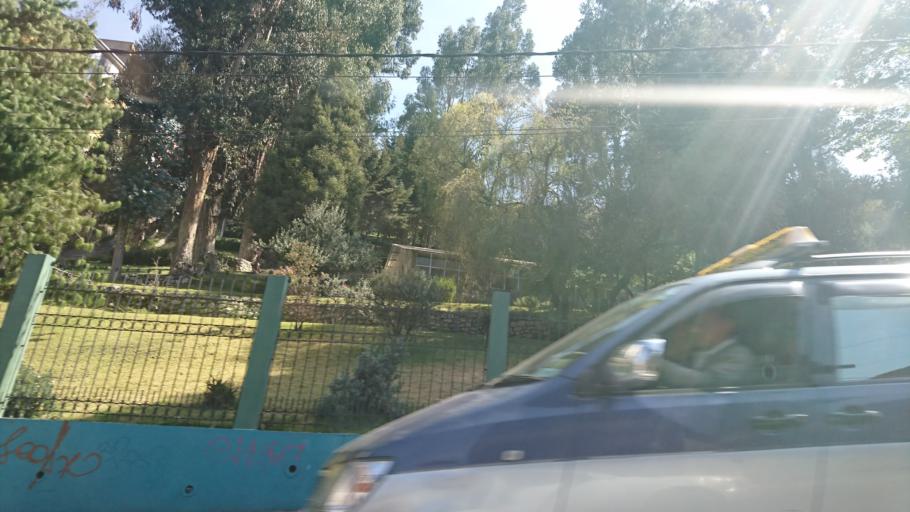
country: BO
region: La Paz
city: La Paz
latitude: -16.5041
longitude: -68.1157
